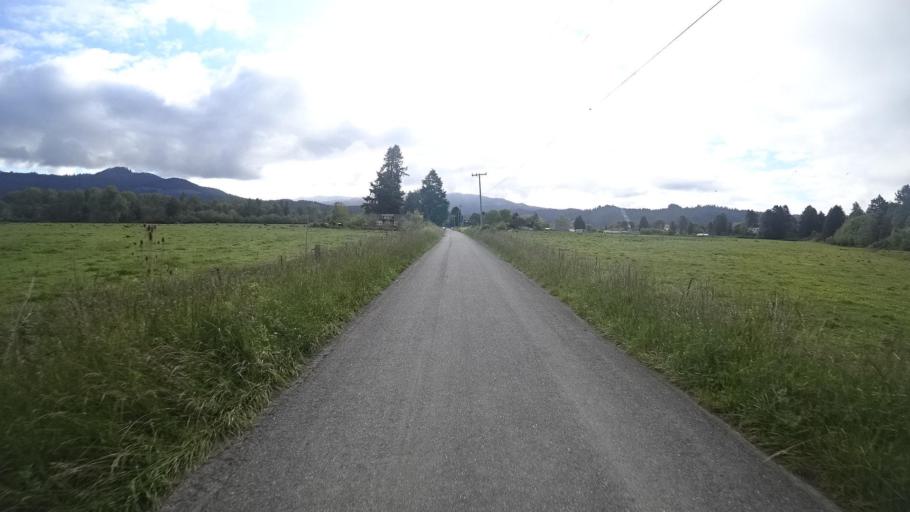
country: US
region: California
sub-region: Humboldt County
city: Blue Lake
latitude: 40.8681
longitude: -124.0014
